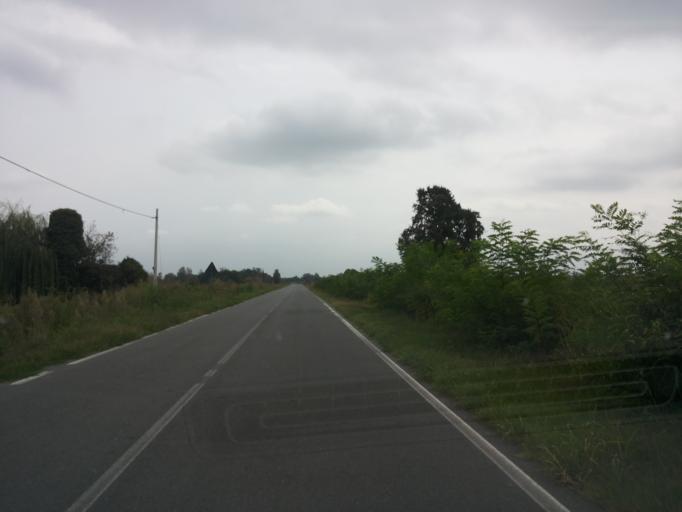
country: IT
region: Piedmont
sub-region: Provincia di Vercelli
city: Prarolo
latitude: 45.3015
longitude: 8.4581
